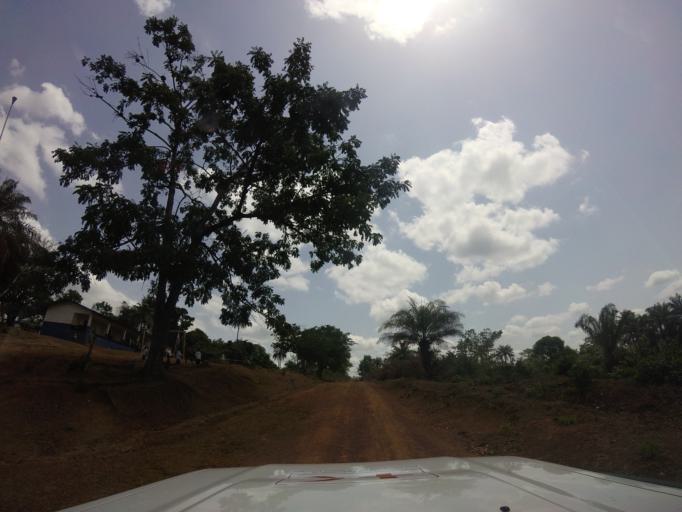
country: SL
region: Southern Province
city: Zimmi
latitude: 7.1654
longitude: -11.2409
